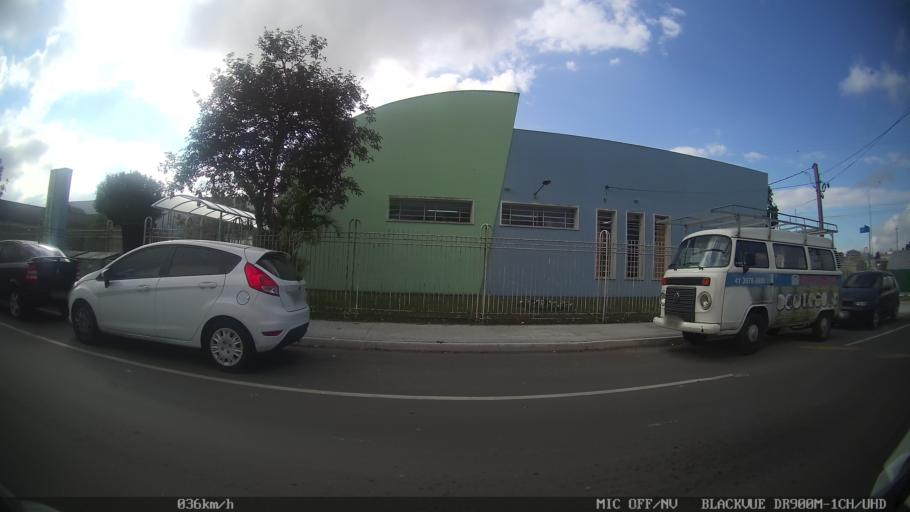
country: BR
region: Parana
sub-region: Pinhais
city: Pinhais
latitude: -25.3958
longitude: -49.1867
